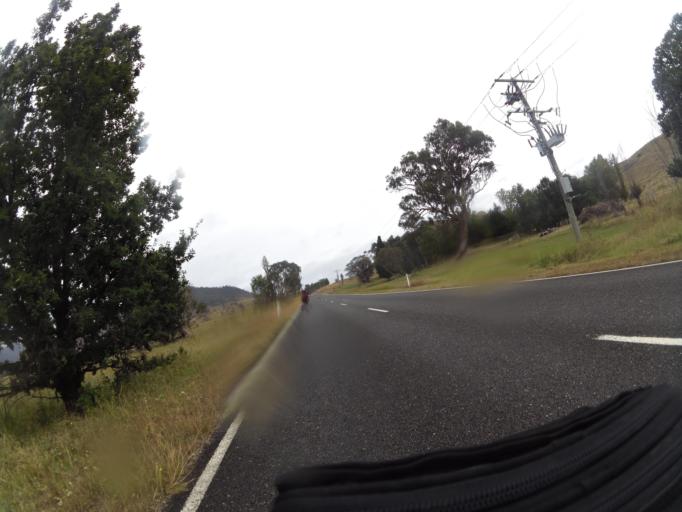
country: AU
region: New South Wales
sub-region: Greater Hume Shire
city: Holbrook
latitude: -36.2115
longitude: 147.7326
